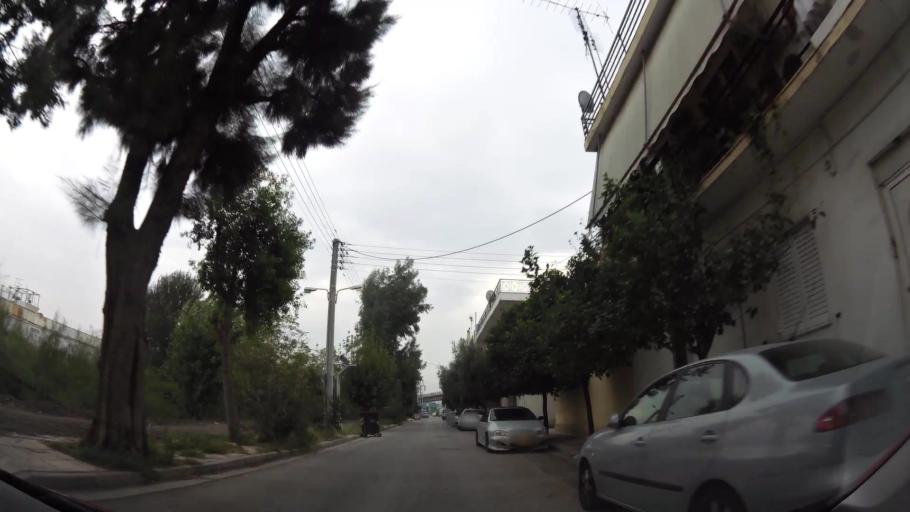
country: GR
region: Attica
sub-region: Nomarchia Athinas
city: Peristeri
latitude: 37.9988
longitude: 23.6947
